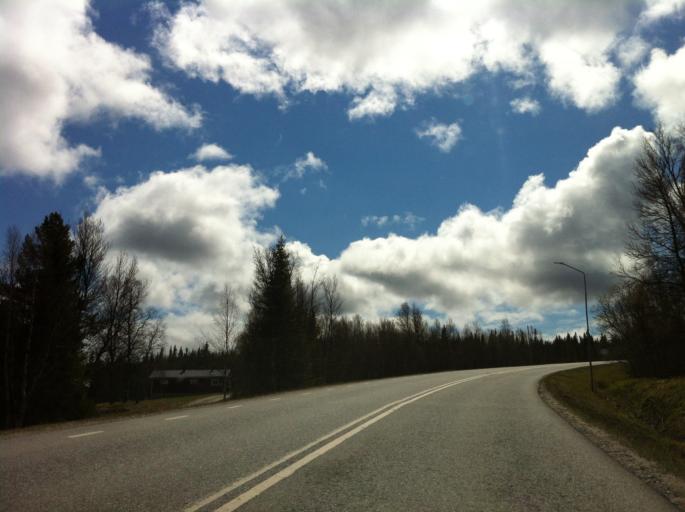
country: NO
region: Hedmark
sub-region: Engerdal
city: Engerdal
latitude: 62.5439
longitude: 12.4689
